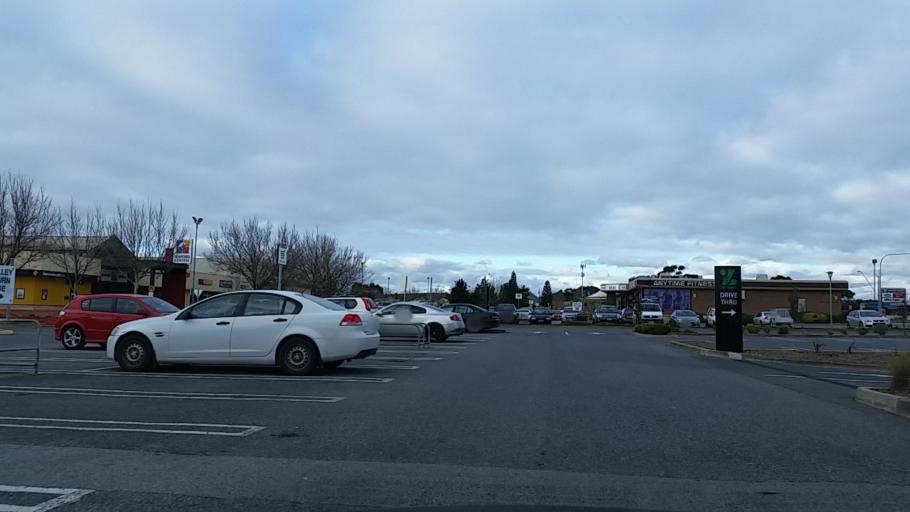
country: AU
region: South Australia
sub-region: Onkaparinga
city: Seaford
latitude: -35.1908
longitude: 138.4783
